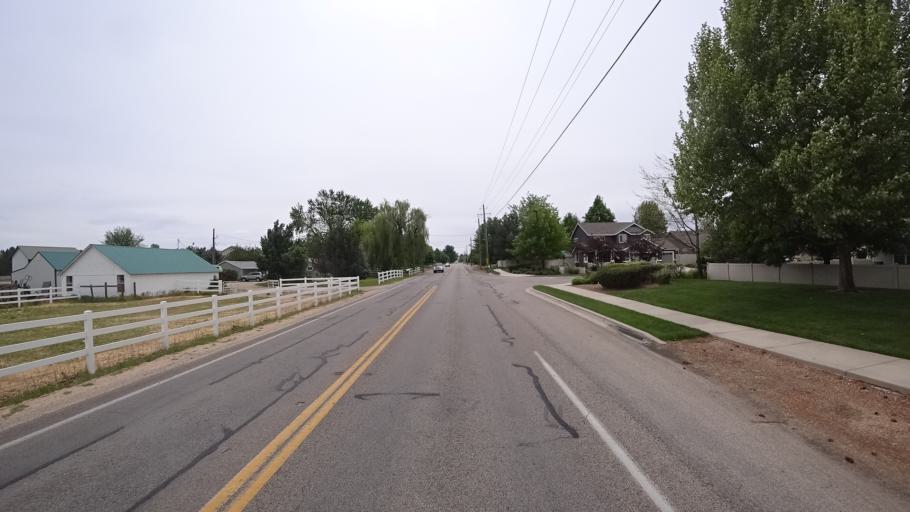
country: US
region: Idaho
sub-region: Ada County
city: Meridian
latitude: 43.5728
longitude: -116.3746
